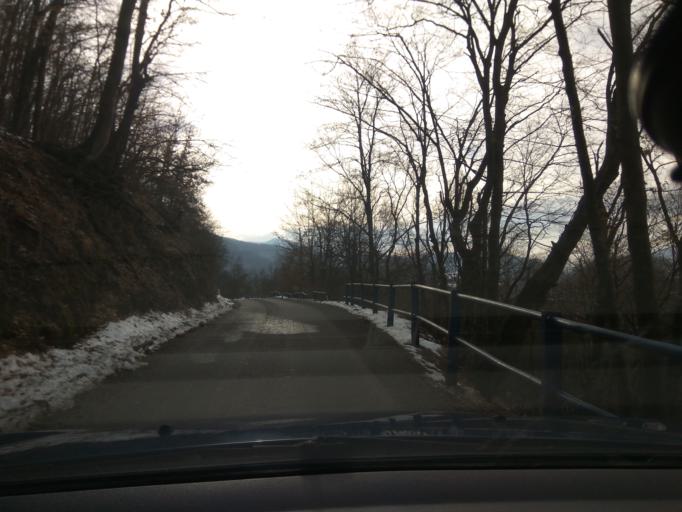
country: SK
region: Banskobystricky
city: Zarnovica
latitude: 48.4835
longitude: 18.7338
